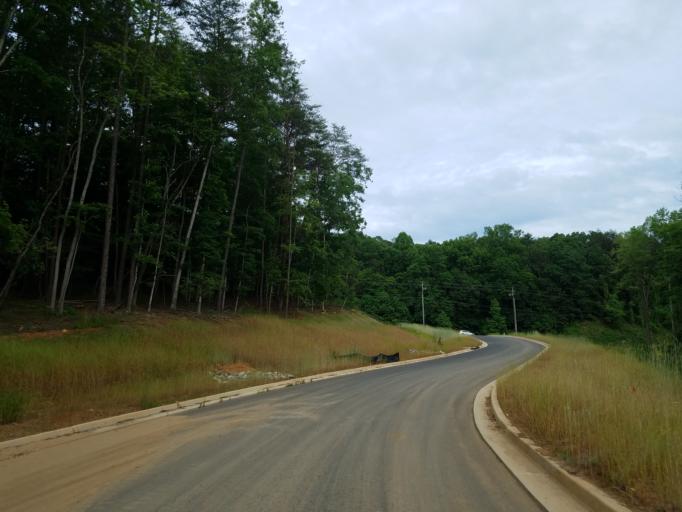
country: US
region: Georgia
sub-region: Lumpkin County
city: Dahlonega
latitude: 34.5170
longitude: -83.9771
